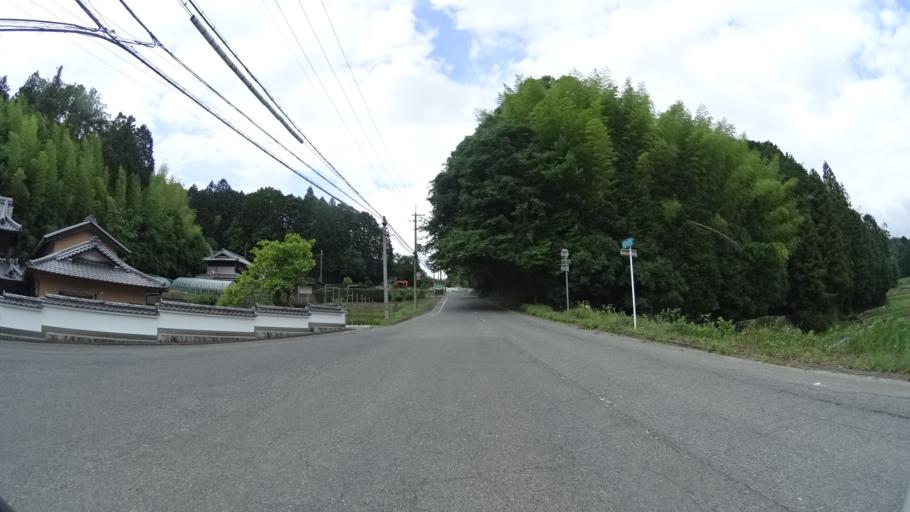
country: JP
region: Nara
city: Nara-shi
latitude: 34.7176
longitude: 135.9022
